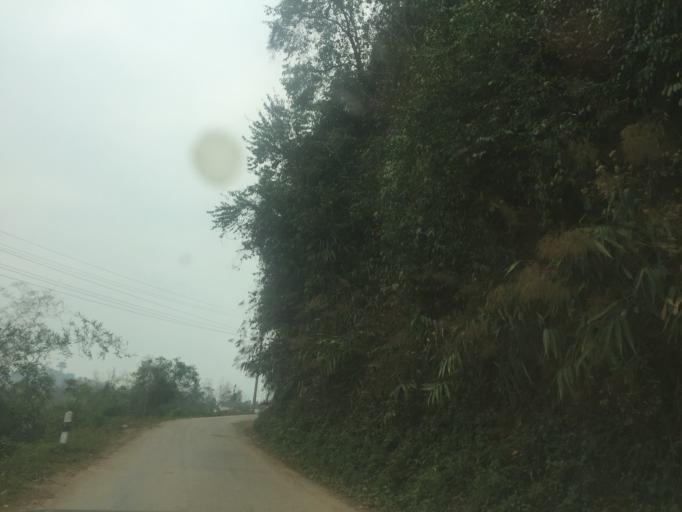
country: LA
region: Vientiane
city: Muang Sanakham
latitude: 18.3876
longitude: 101.5242
